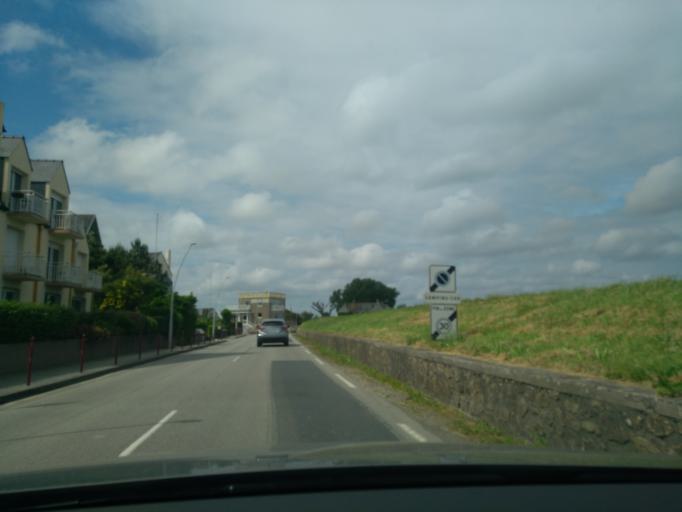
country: FR
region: Lower Normandy
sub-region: Departement de la Manche
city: Saint-Vaast-la-Hougue
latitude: 49.5919
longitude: -1.2668
